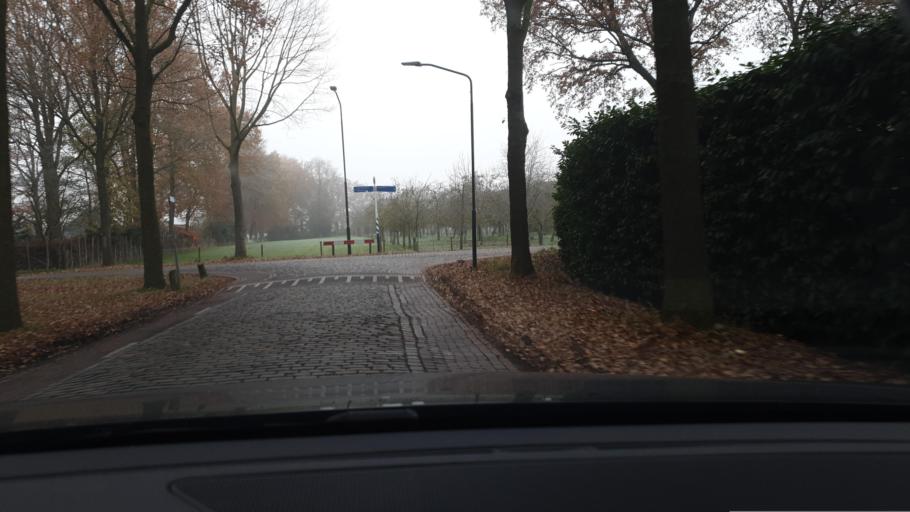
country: NL
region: North Brabant
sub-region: Gemeente Bladel en Netersel
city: Bladel
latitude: 51.3901
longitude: 5.1868
